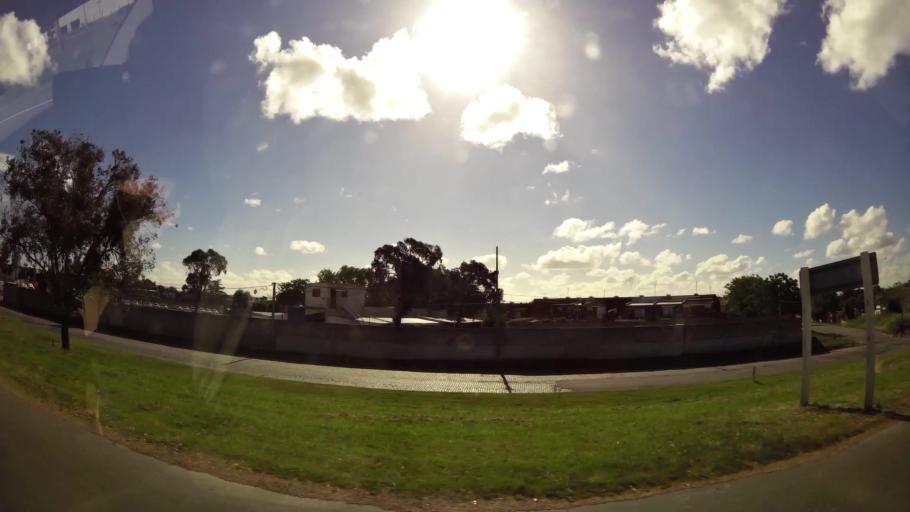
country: UY
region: Canelones
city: La Paz
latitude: -34.8401
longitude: -56.2541
